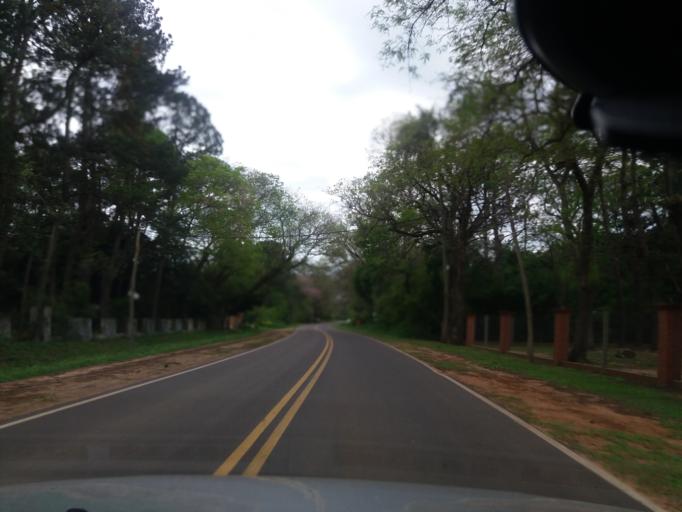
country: AR
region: Corrientes
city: Riachuelo
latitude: -27.4568
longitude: -58.6834
